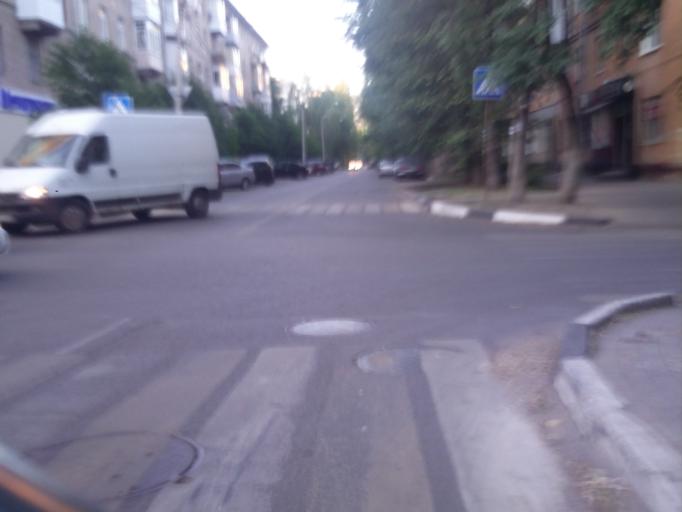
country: RU
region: Voronezj
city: Voronezh
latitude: 51.6502
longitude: 39.1699
